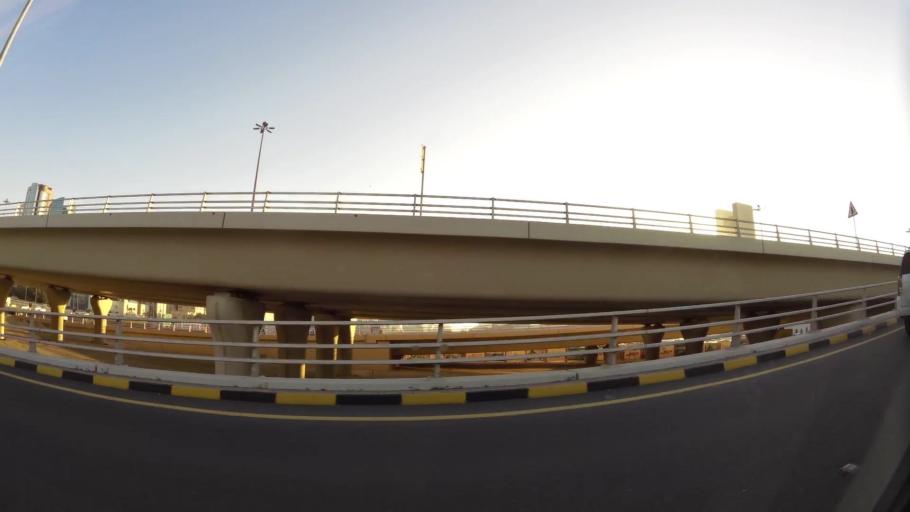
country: BH
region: Muharraq
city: Al Muharraq
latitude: 26.2478
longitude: 50.5890
